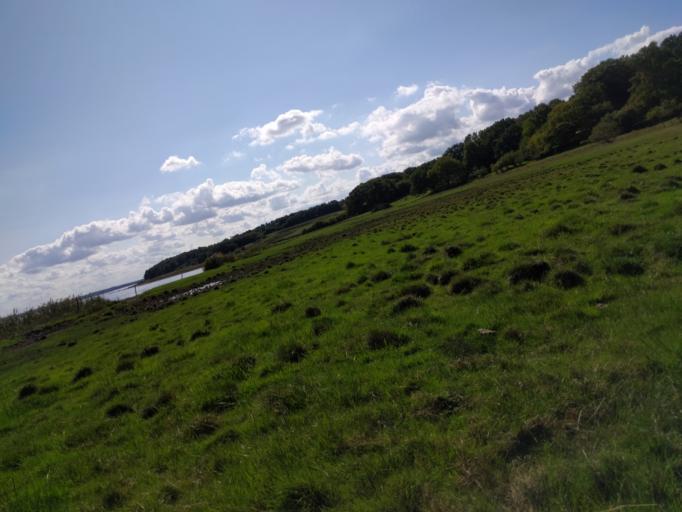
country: DK
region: Central Jutland
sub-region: Skive Kommune
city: Hojslev
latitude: 56.6650
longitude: 9.0947
